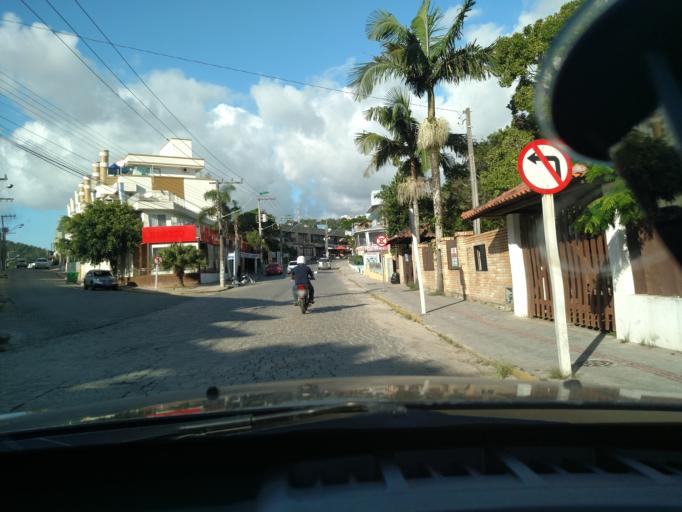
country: BR
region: Santa Catarina
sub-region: Porto Belo
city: Porto Belo
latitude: -27.1489
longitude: -48.4839
